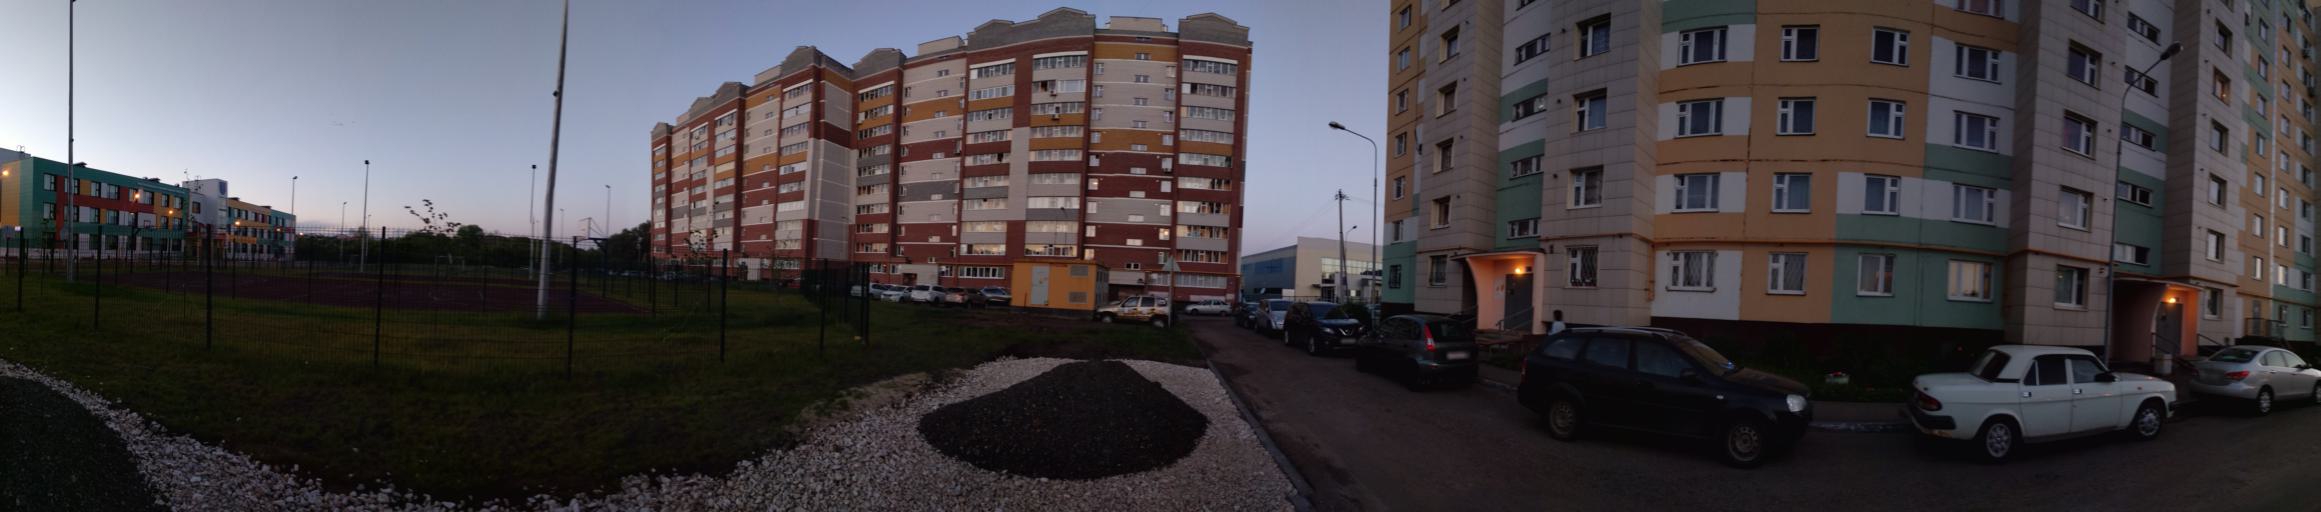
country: RU
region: Tatarstan
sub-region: Gorod Kazan'
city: Kazan
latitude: 55.8049
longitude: 49.2120
